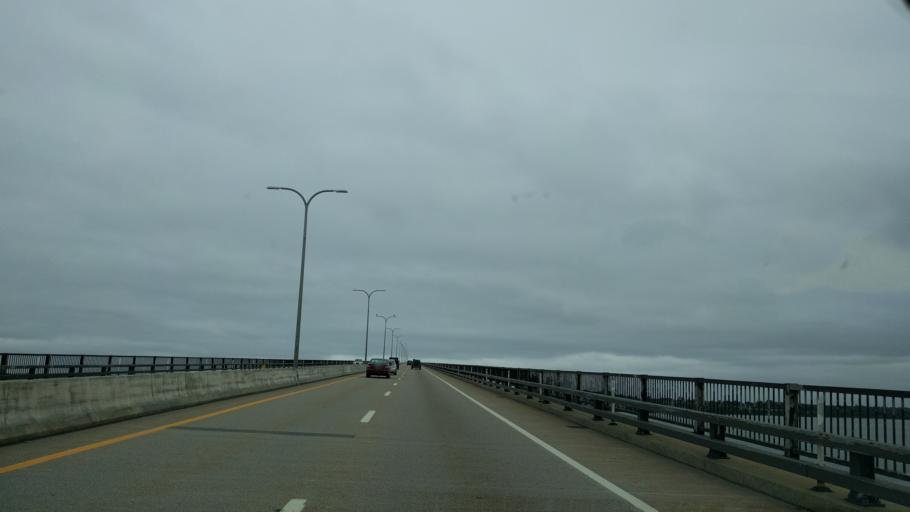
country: US
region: Rhode Island
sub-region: Newport County
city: Jamestown
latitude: 41.5291
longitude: -71.4071
